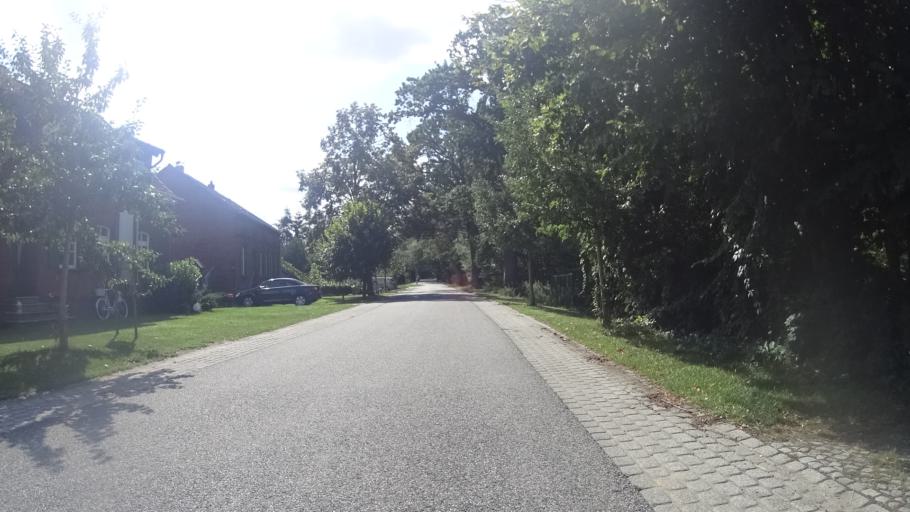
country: DE
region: Brandenburg
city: Ruhstadt
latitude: 52.9171
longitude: 11.8687
